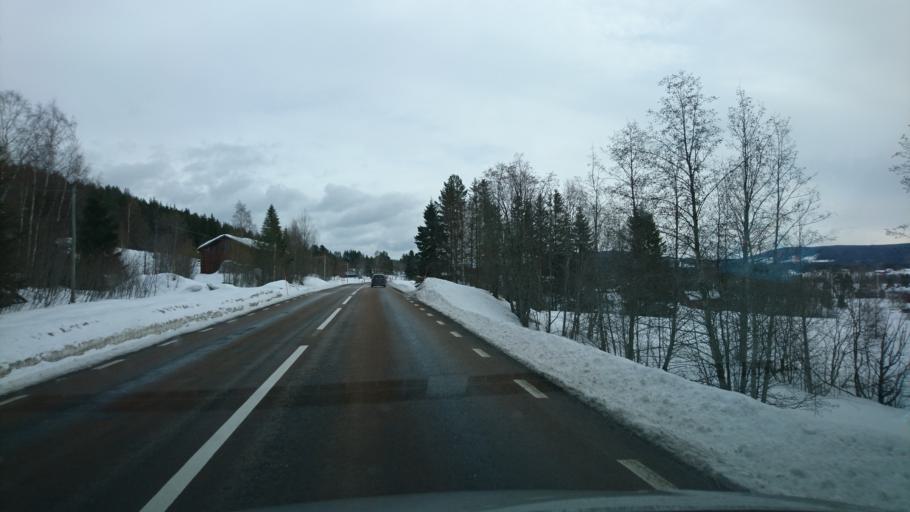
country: SE
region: Vaesternorrland
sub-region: Solleftea Kommun
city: Solleftea
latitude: 63.1752
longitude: 16.9147
